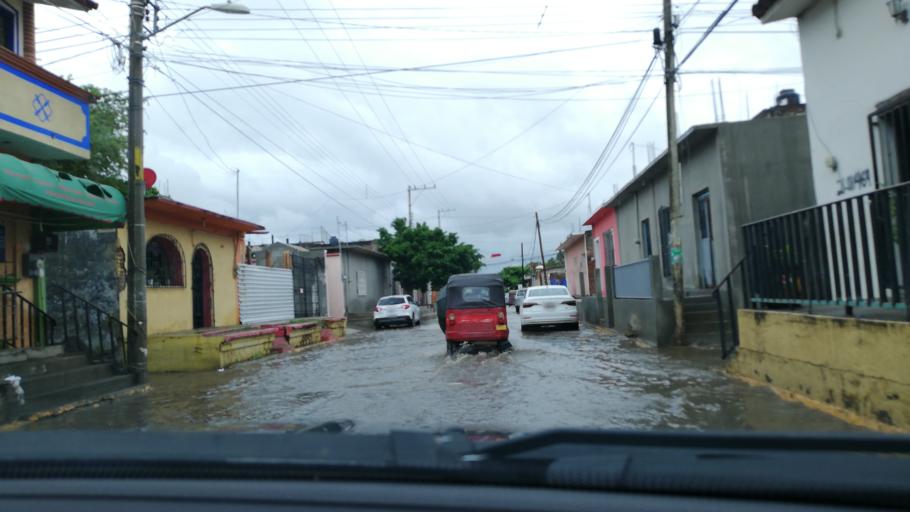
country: MX
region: Oaxaca
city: Juchitan de Zaragoza
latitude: 16.4346
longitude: -95.0177
